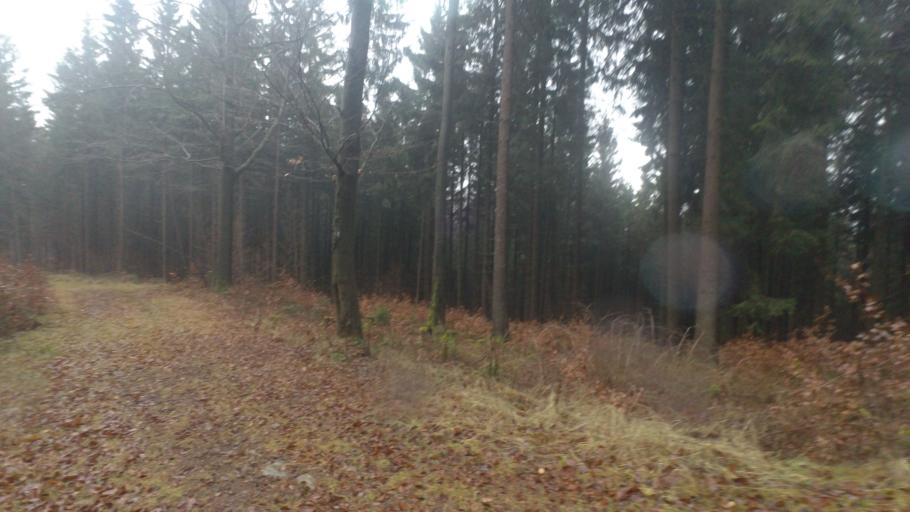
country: DE
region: Thuringia
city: Frankenhain
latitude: 50.7235
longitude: 10.7879
